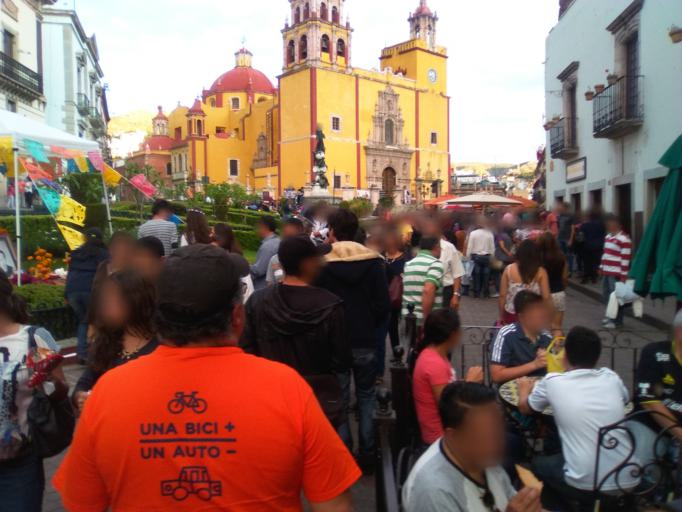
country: MX
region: Guanajuato
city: Guanajuato
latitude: 21.0169
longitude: -101.2542
